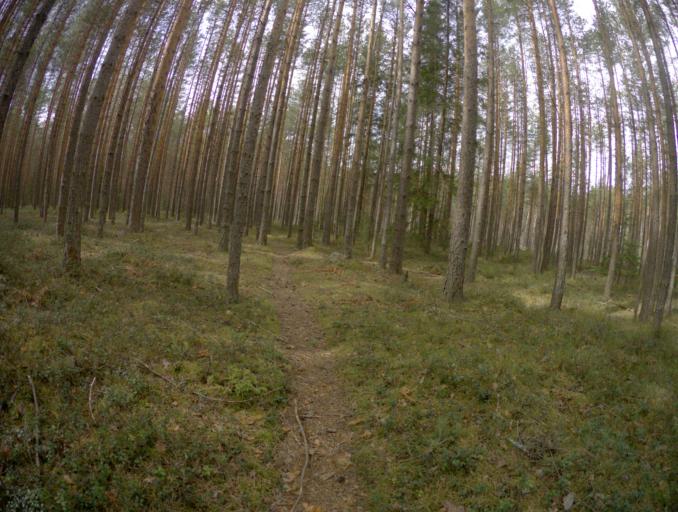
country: RU
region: Vladimir
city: Raduzhnyy
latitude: 55.9485
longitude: 40.2714
